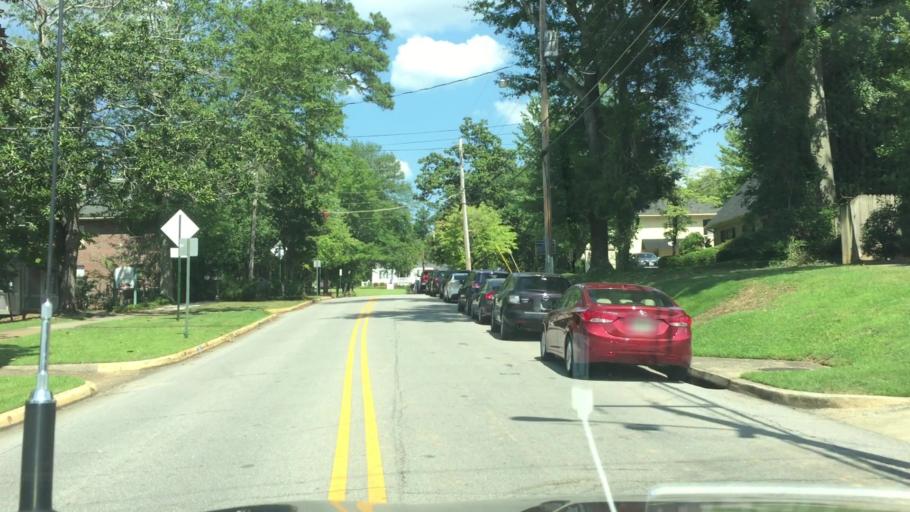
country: US
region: Alabama
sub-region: Lee County
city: Auburn
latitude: 32.6066
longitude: -85.4748
